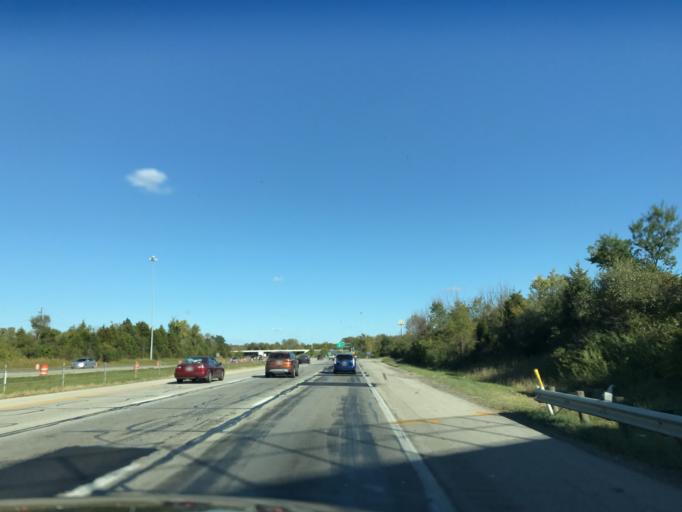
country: US
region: Ohio
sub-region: Franklin County
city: Obetz
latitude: 39.8714
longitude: -82.9418
